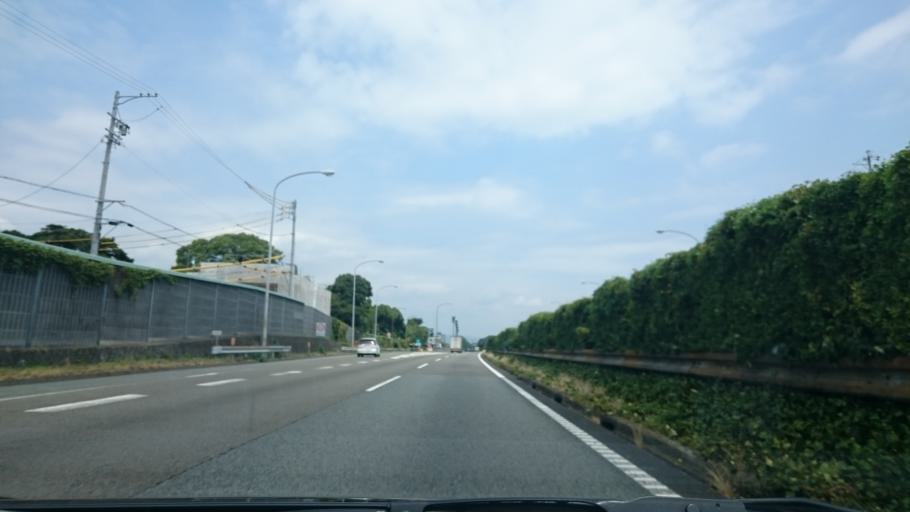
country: JP
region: Shizuoka
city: Shizuoka-shi
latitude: 34.9804
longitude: 138.4324
